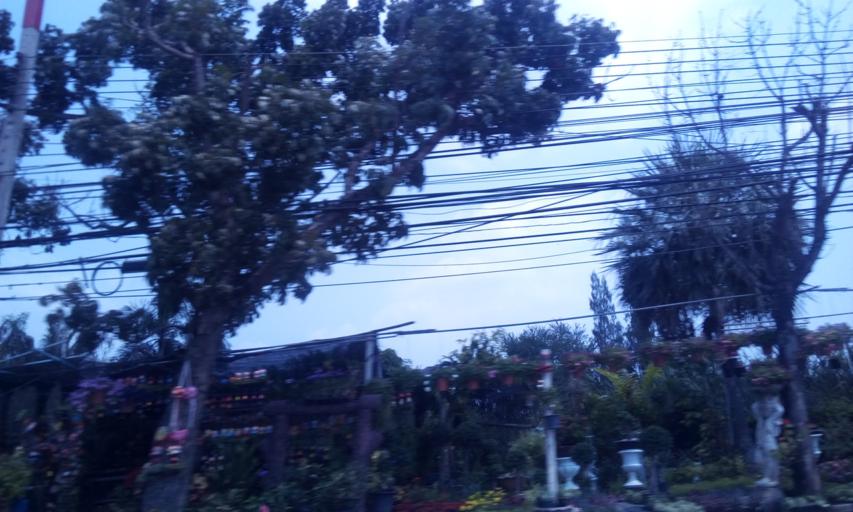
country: TH
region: Chachoengsao
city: Chachoengsao
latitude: 13.6758
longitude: 101.0838
